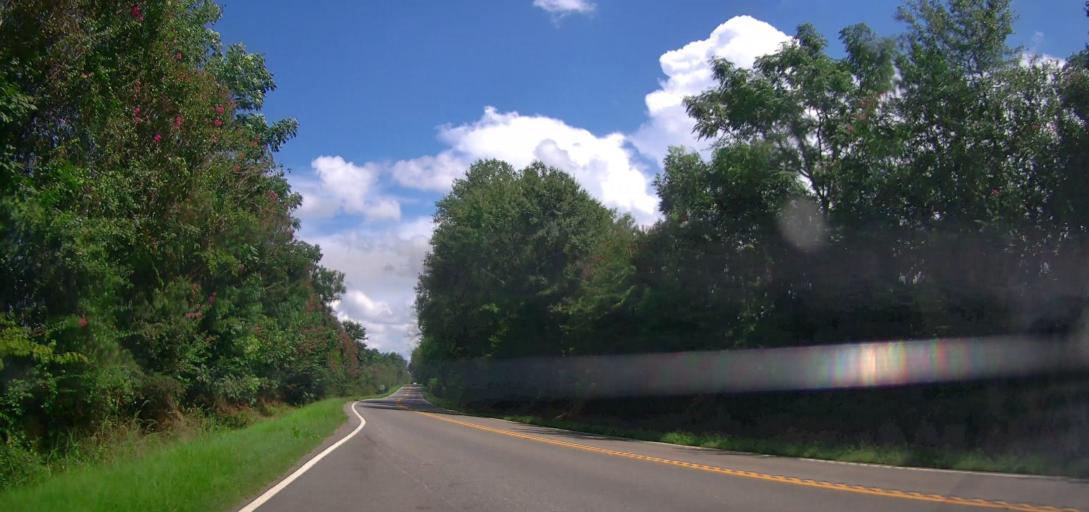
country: US
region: Georgia
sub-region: Macon County
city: Marshallville
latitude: 32.4485
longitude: -83.9806
